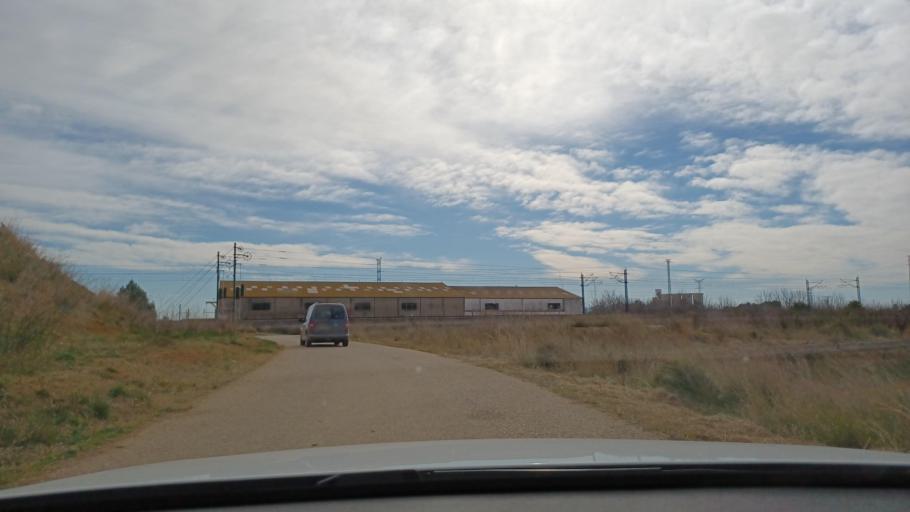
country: ES
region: Valencia
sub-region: Provincia de Valencia
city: Benifaio
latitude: 39.2921
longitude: -0.4382
